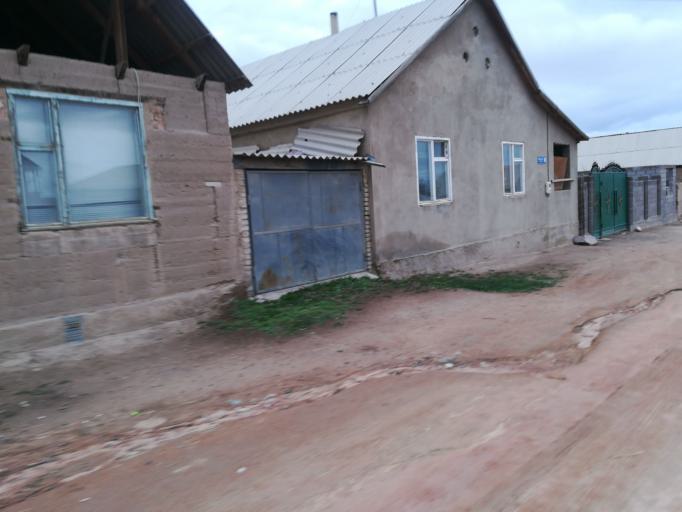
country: KG
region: Ysyk-Koel
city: Bokombayevskoye
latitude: 42.1133
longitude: 76.9817
